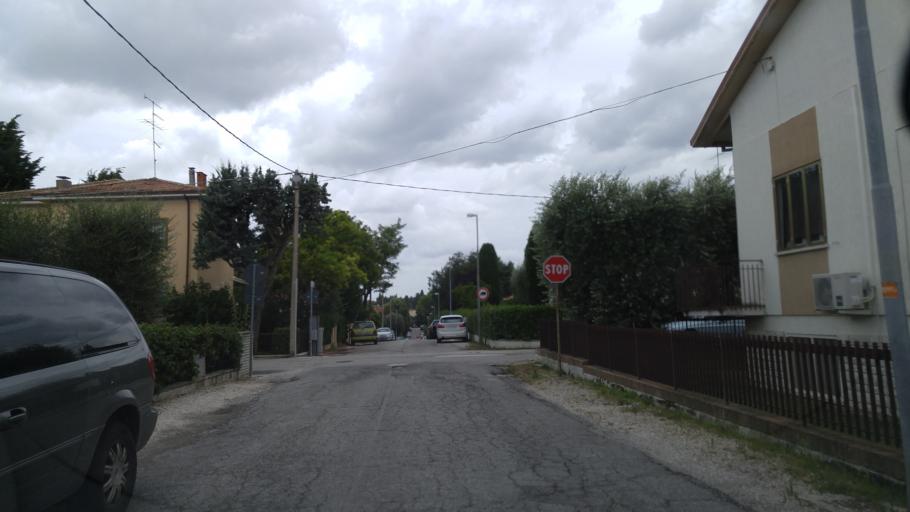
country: IT
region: The Marches
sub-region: Provincia di Pesaro e Urbino
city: Fano
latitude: 43.8480
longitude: 13.0049
